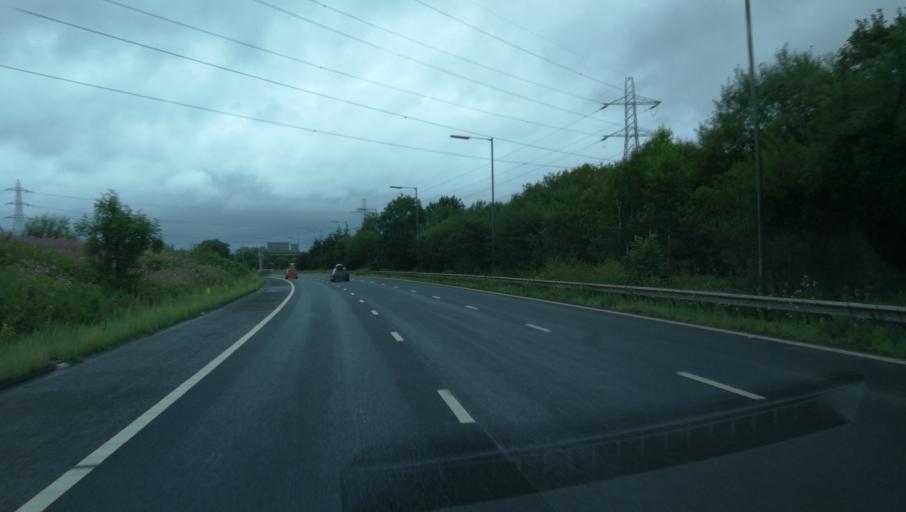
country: GB
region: England
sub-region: Borough of Bolton
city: Kearsley
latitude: 53.5357
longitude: -2.3923
